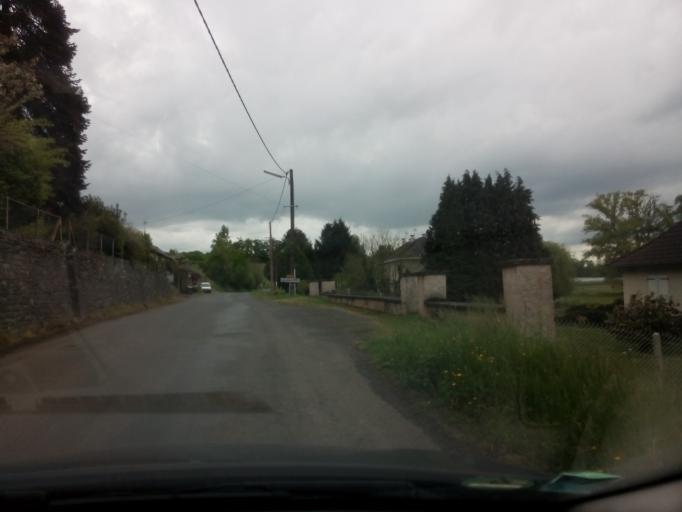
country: FR
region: Limousin
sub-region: Departement de la Correze
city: Allassac
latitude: 45.2714
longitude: 1.4634
